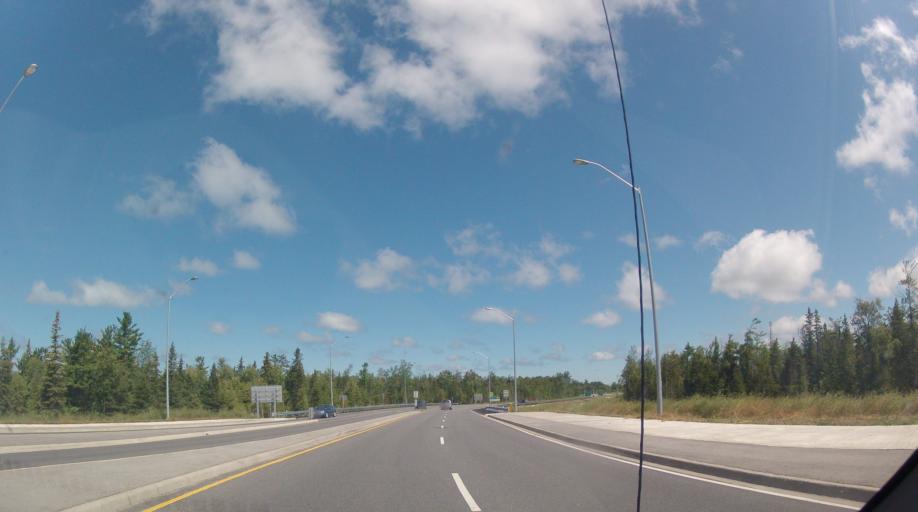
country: CA
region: Ontario
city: Collingwood
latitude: 44.4624
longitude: -80.1126
